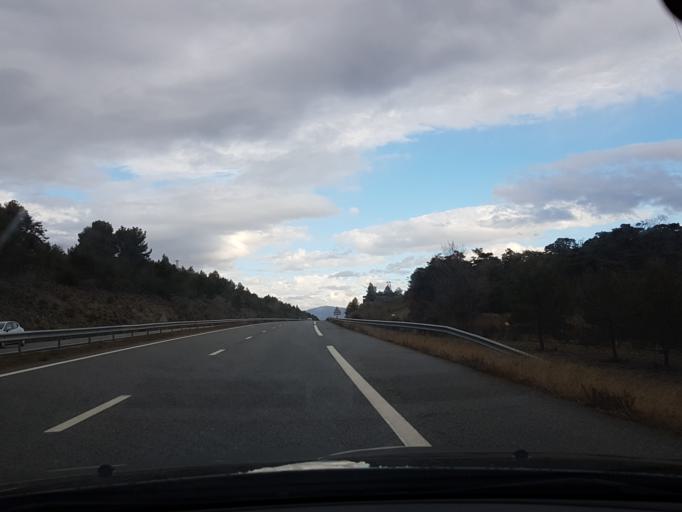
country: FR
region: Provence-Alpes-Cote d'Azur
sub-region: Departement des Alpes-de-Haute-Provence
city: Les Mees
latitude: 44.0768
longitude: 5.9811
